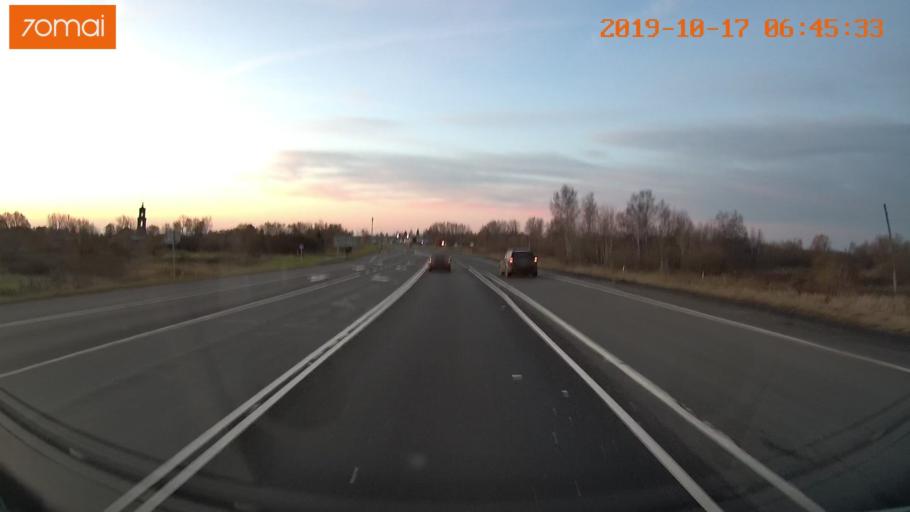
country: RU
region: Vladimir
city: Kideksha
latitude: 56.5586
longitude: 40.5481
